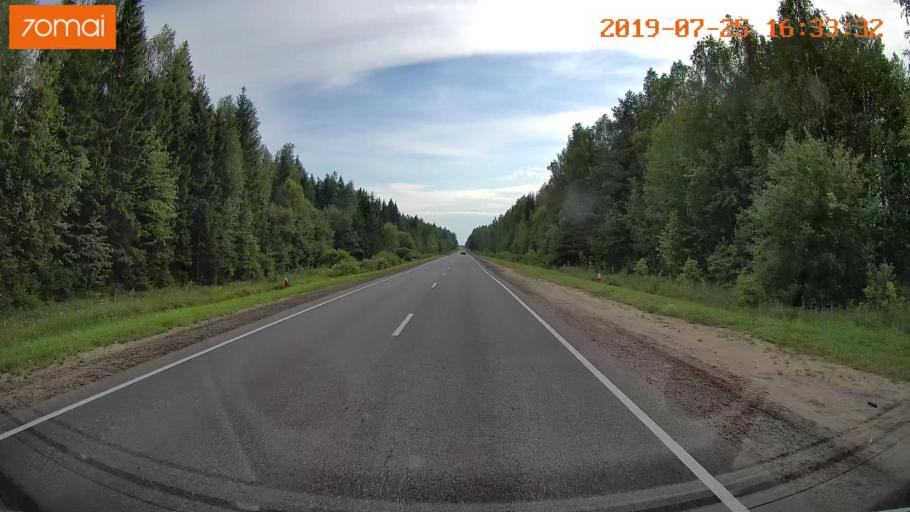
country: RU
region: Ivanovo
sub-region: Privolzhskiy Rayon
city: Ples
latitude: 57.4262
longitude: 41.4548
